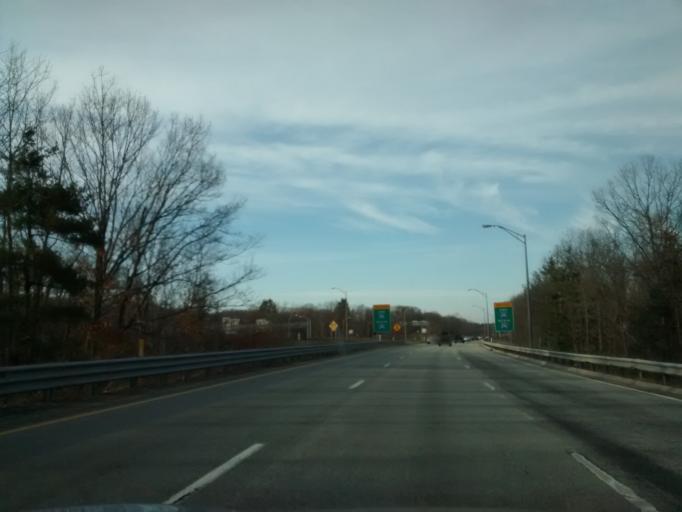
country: US
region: Massachusetts
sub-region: Worcester County
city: Auburn
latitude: 42.1874
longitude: -71.8472
